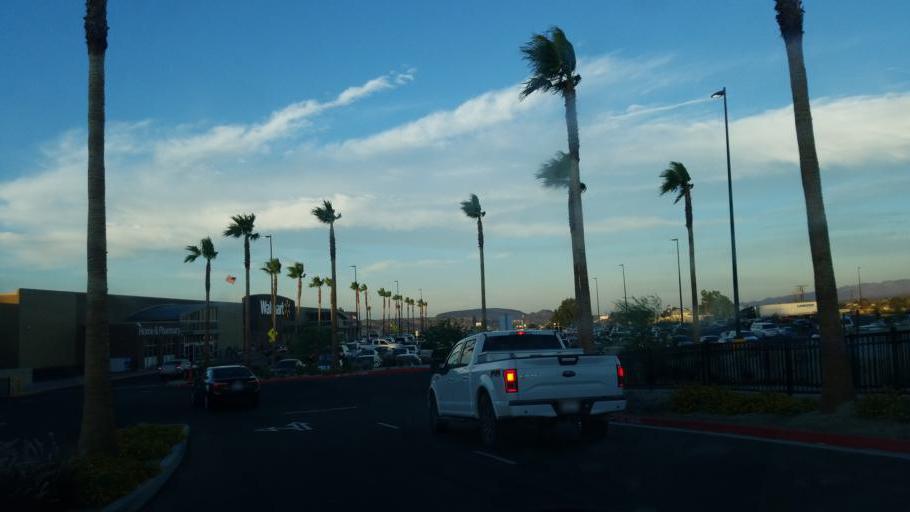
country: US
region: California
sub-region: San Bernardino County
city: Barstow
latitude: 34.8839
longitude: -116.9932
